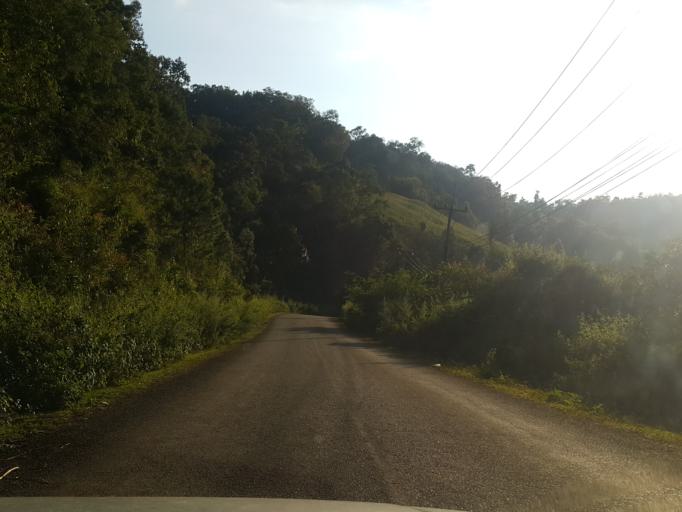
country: TH
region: Chiang Mai
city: Mae Chaem
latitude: 18.7450
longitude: 98.2137
